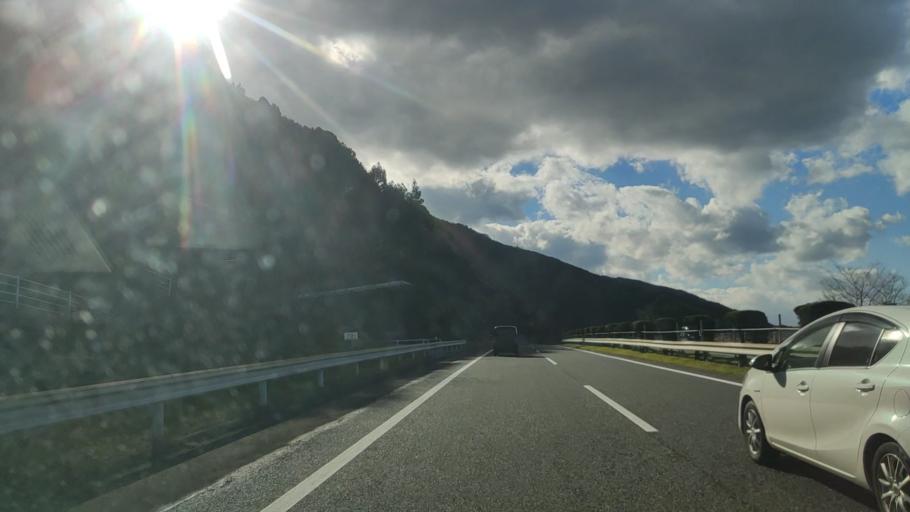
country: JP
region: Ehime
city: Niihama
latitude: 33.9381
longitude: 133.3814
